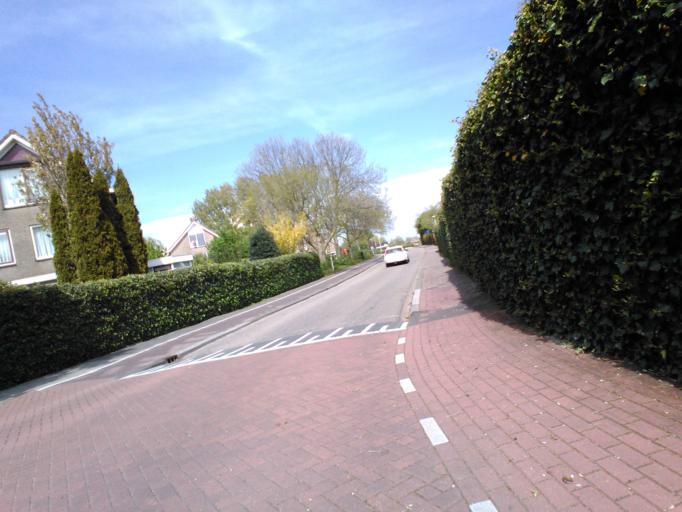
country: NL
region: South Holland
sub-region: Bodegraven-Reeuwijk
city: Reeuwijk
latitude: 52.0480
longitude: 4.7316
